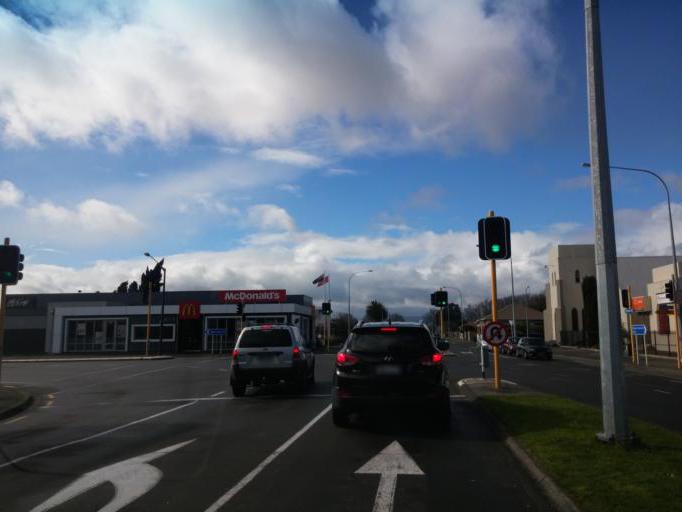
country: NZ
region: Manawatu-Wanganui
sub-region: Palmerston North City
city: Palmerston North
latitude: -40.3576
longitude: 175.6176
